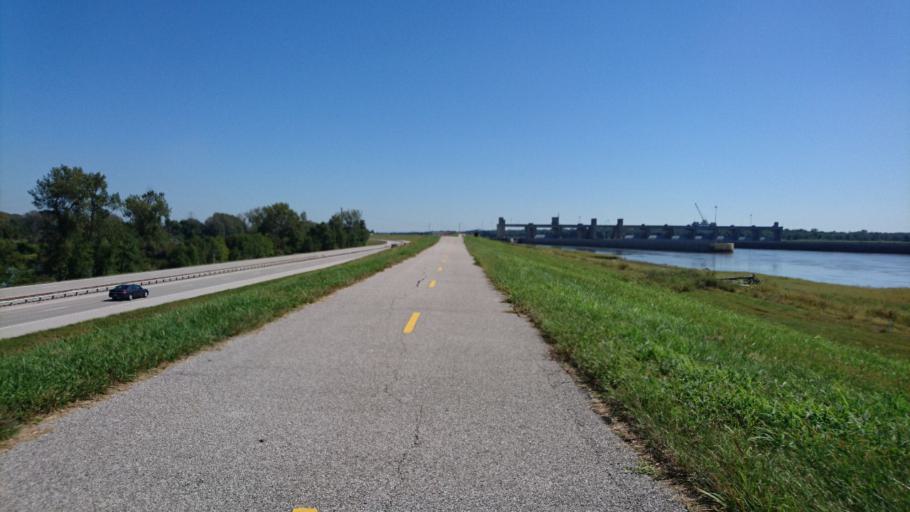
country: US
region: Illinois
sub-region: Madison County
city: Alton
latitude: 38.8763
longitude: -90.1577
